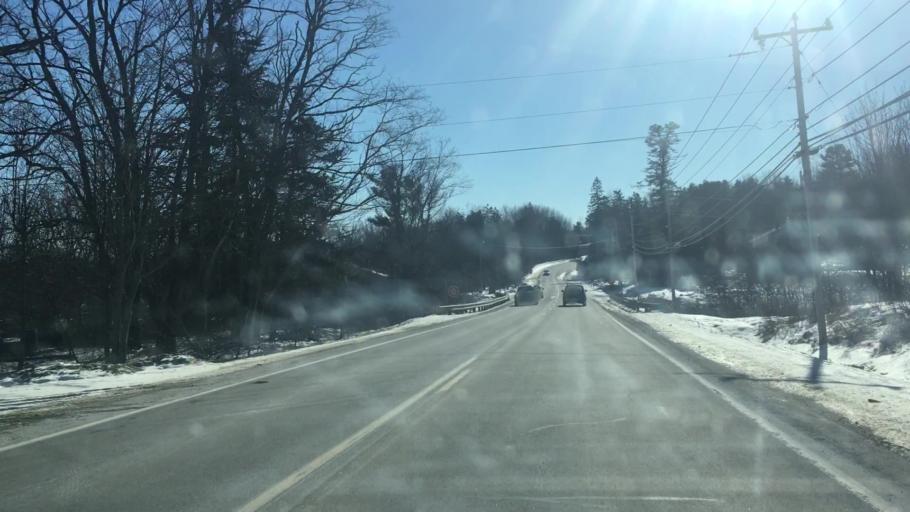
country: US
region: Maine
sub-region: Hancock County
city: Ellsworth
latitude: 44.5229
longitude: -68.4313
